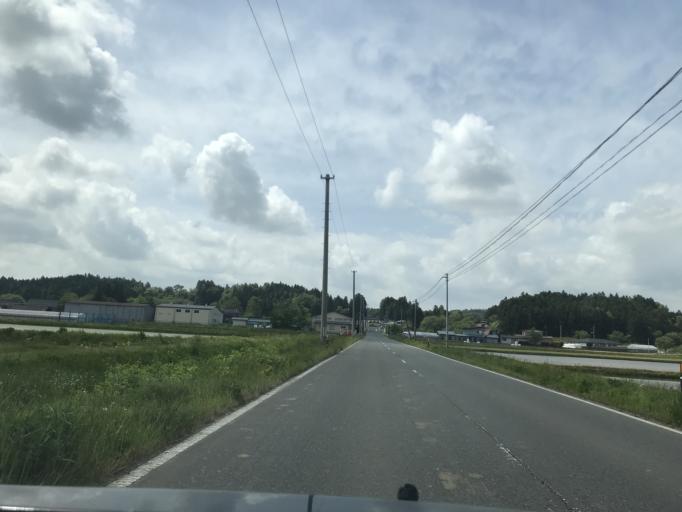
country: JP
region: Iwate
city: Ichinoseki
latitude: 38.7938
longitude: 141.0046
